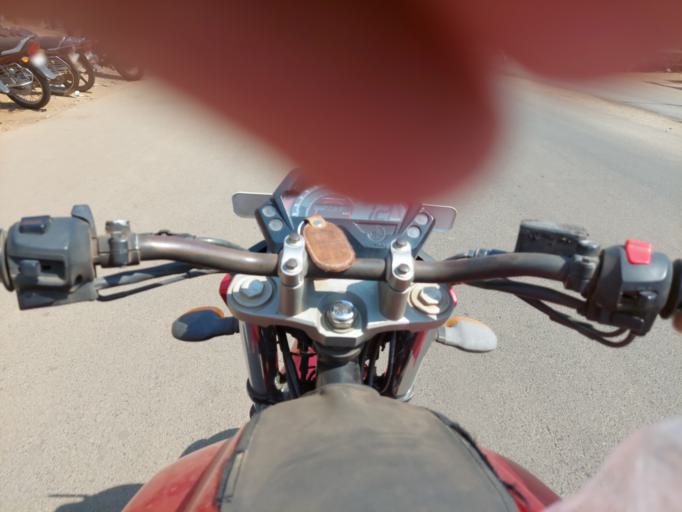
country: IN
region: Telangana
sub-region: Rangareddi
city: Vikarabad
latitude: 17.3362
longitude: 77.9045
